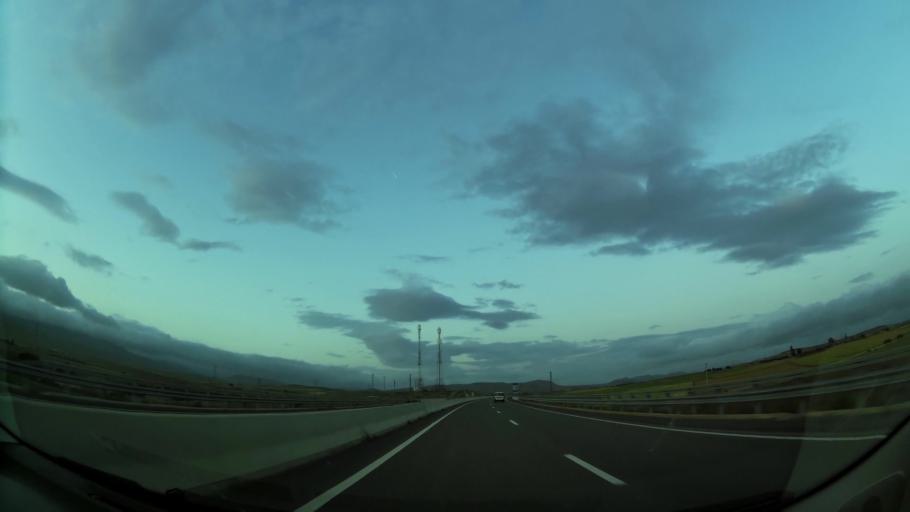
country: MA
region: Oriental
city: El Aioun
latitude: 34.6230
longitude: -2.5435
